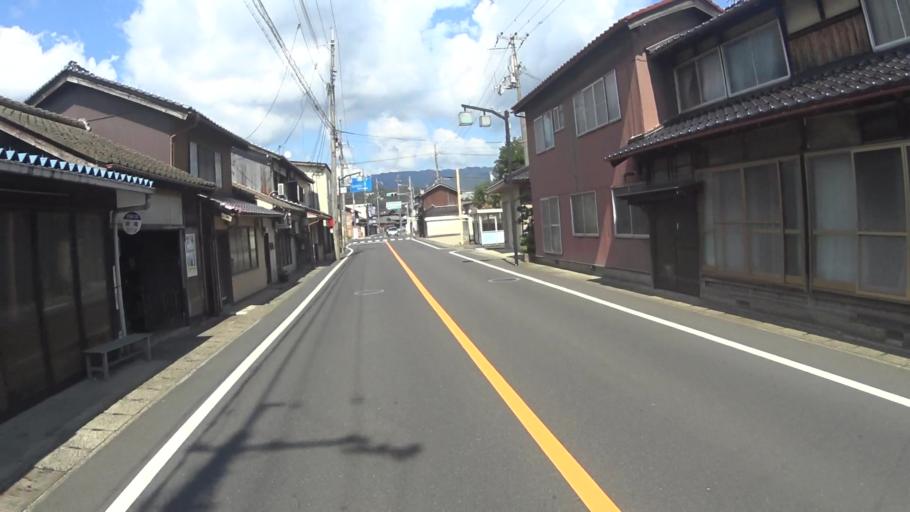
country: JP
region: Kyoto
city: Miyazu
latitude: 35.5645
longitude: 135.1522
